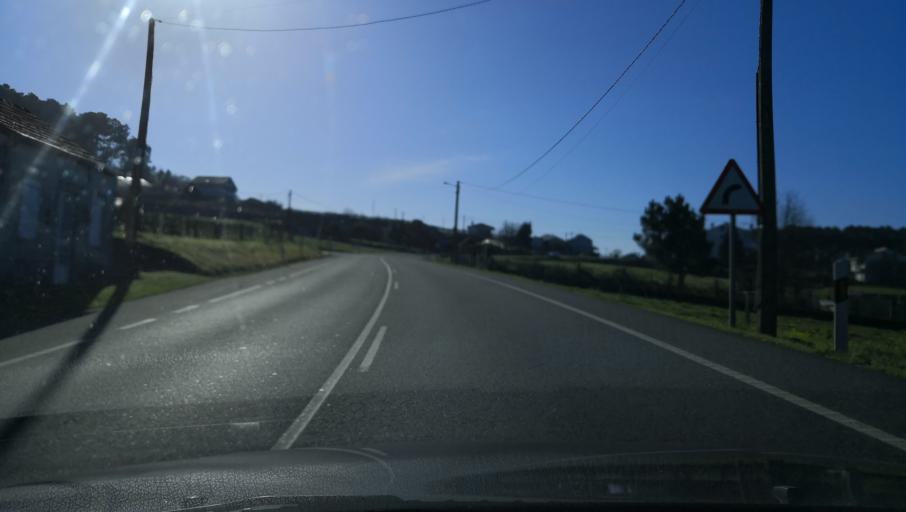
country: ES
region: Galicia
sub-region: Provincia da Coruna
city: Ribeira
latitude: 42.7636
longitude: -8.3998
